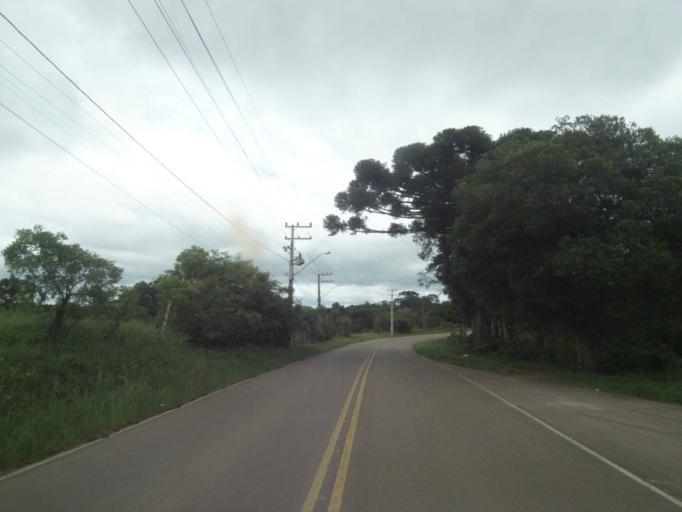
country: BR
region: Parana
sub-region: Campina Grande Do Sul
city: Campina Grande do Sul
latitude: -25.3108
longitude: -49.0386
